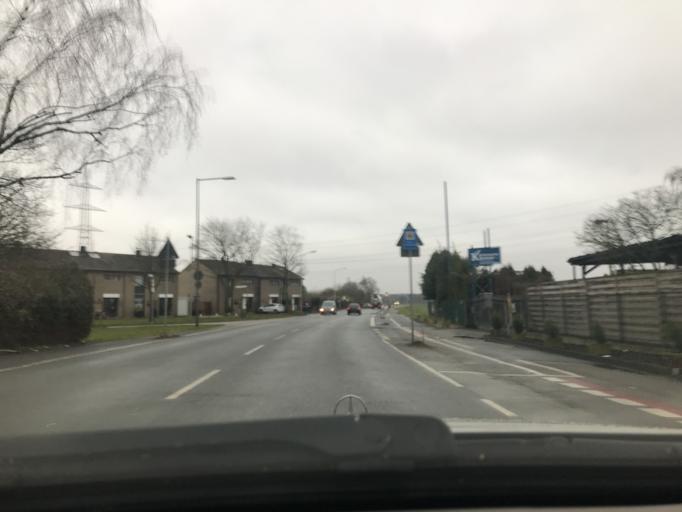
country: DE
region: North Rhine-Westphalia
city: Tonisvorst
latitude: 51.3127
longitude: 6.5327
